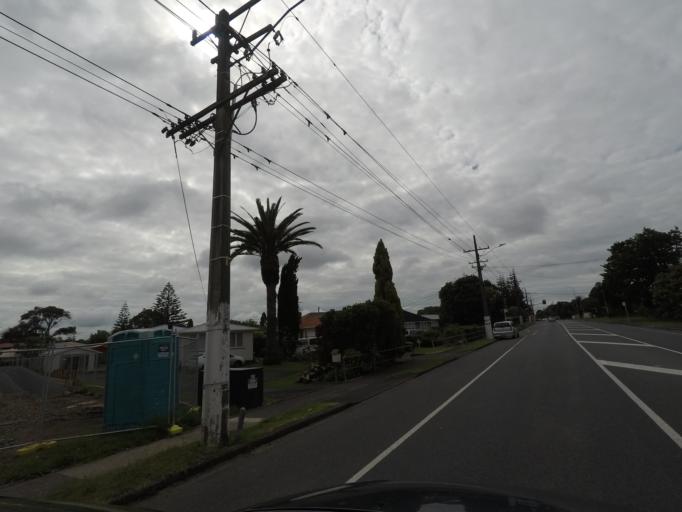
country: NZ
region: Auckland
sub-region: Auckland
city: Rosebank
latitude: -36.8701
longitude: 174.6191
